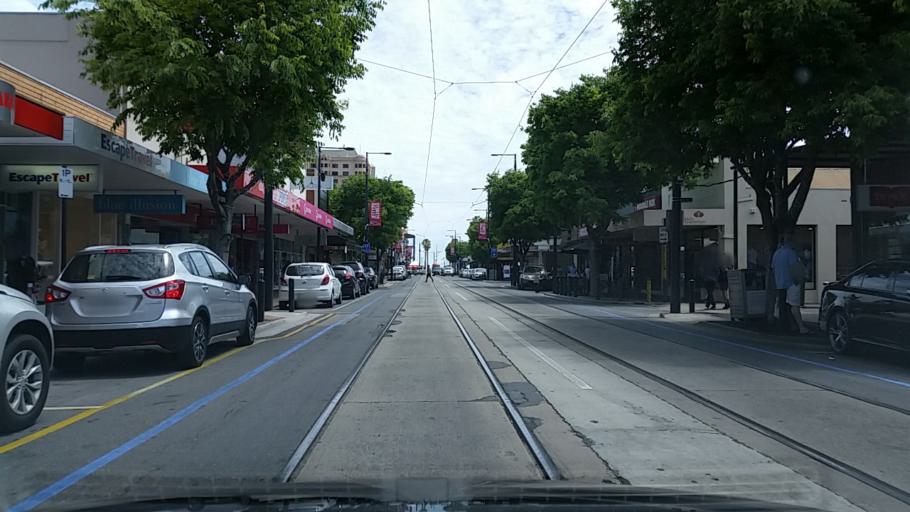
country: AU
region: South Australia
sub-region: Adelaide
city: Glenelg
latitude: -34.9803
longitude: 138.5147
